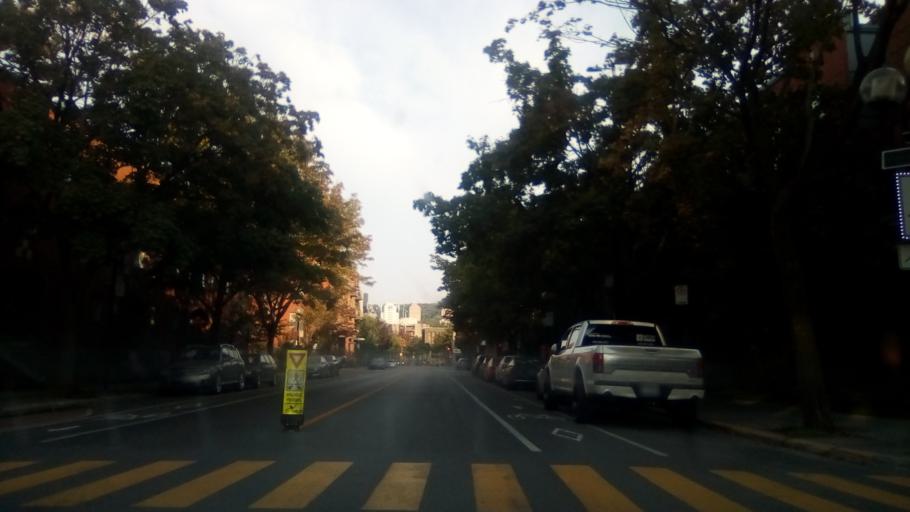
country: CA
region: Quebec
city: Westmount
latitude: 45.4815
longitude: -73.5743
